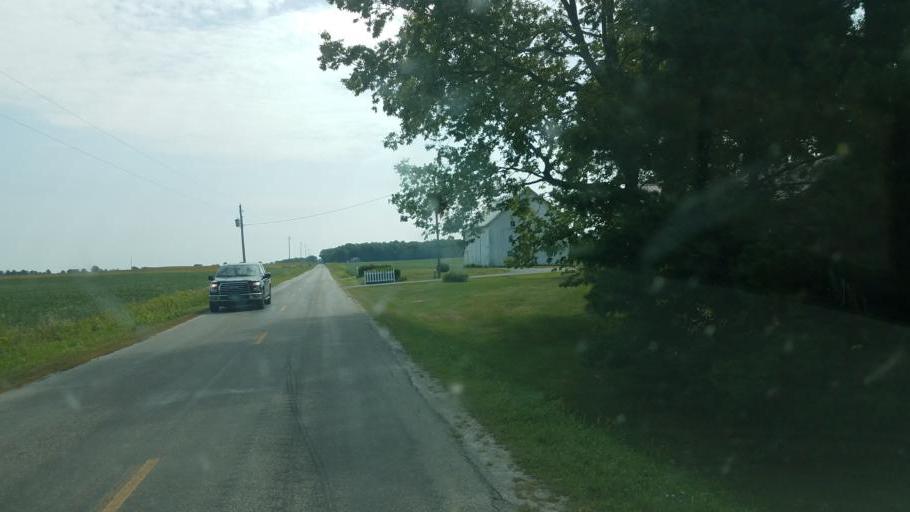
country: US
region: Ohio
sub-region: Delaware County
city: Ashley
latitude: 40.4577
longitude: -83.0522
